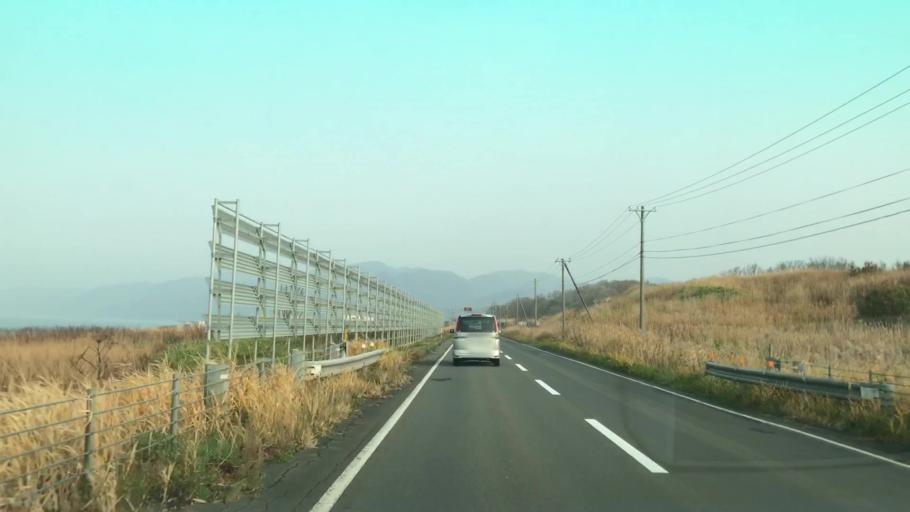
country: JP
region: Hokkaido
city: Ishikari
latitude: 43.3727
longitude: 141.4269
